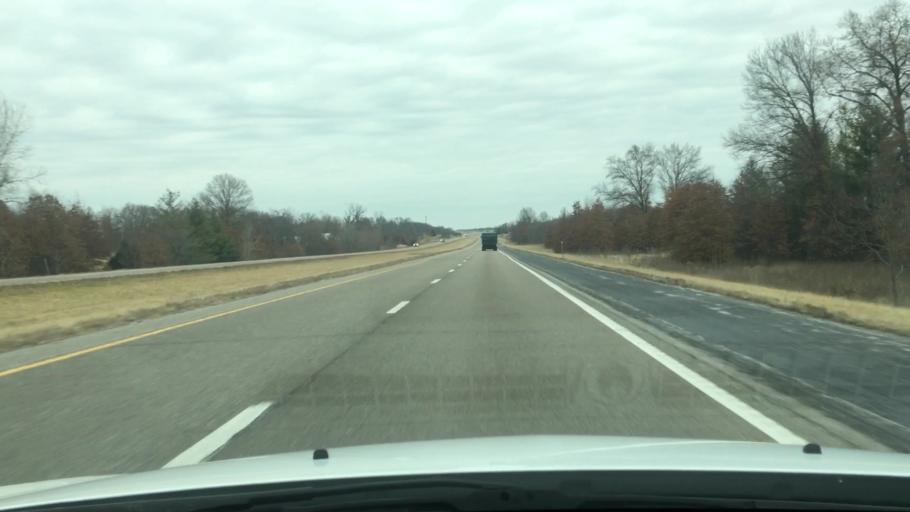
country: US
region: Missouri
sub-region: Audrain County
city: Mexico
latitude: 39.0440
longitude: -91.8934
